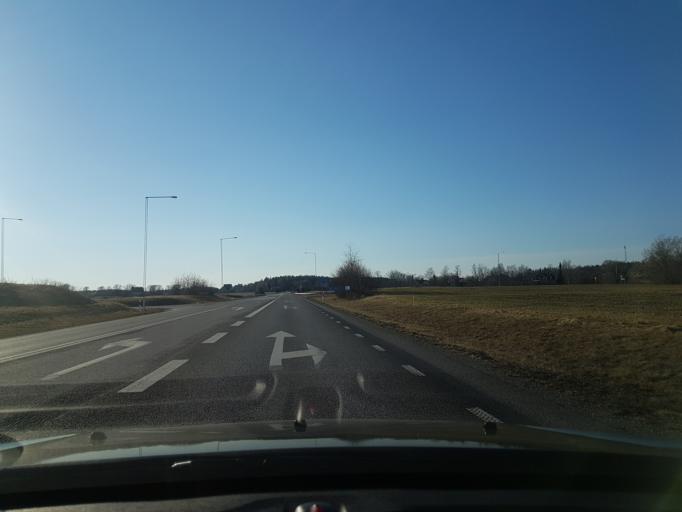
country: SE
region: Uppsala
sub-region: Enkopings Kommun
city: Orsundsbro
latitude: 59.8555
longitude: 17.4308
